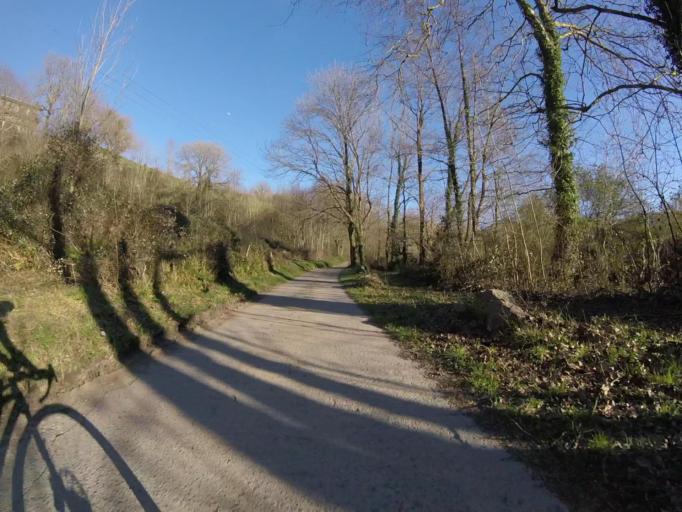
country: ES
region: Basque Country
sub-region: Provincia de Guipuzcoa
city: Errenteria
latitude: 43.2897
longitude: -1.8740
